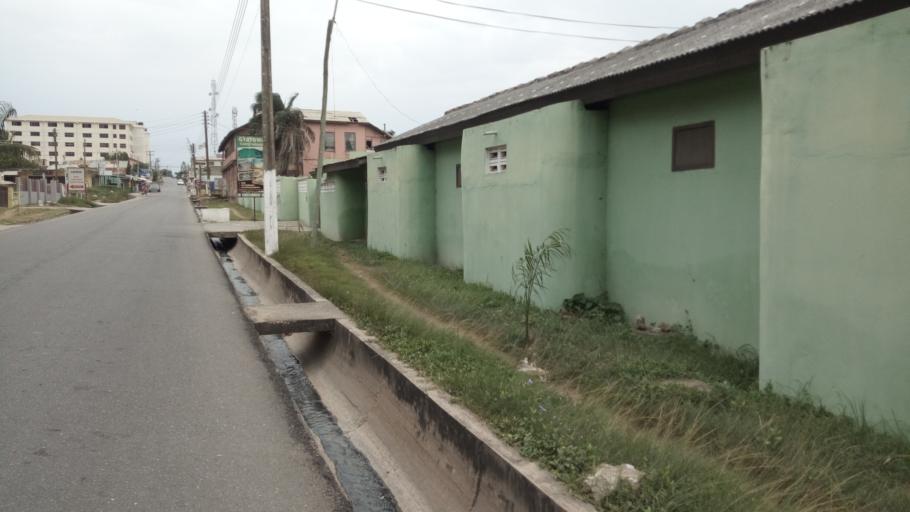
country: GH
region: Central
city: Winneba
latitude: 5.3468
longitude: -0.6281
